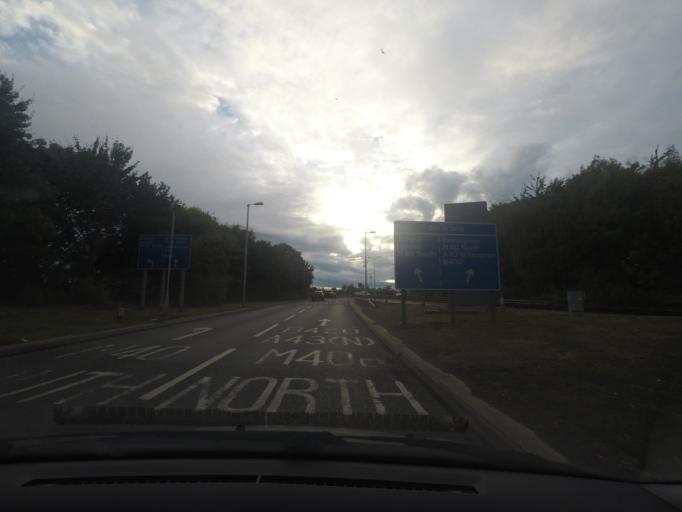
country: GB
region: England
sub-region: Oxfordshire
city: Bicester
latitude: 51.9483
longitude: -1.2022
